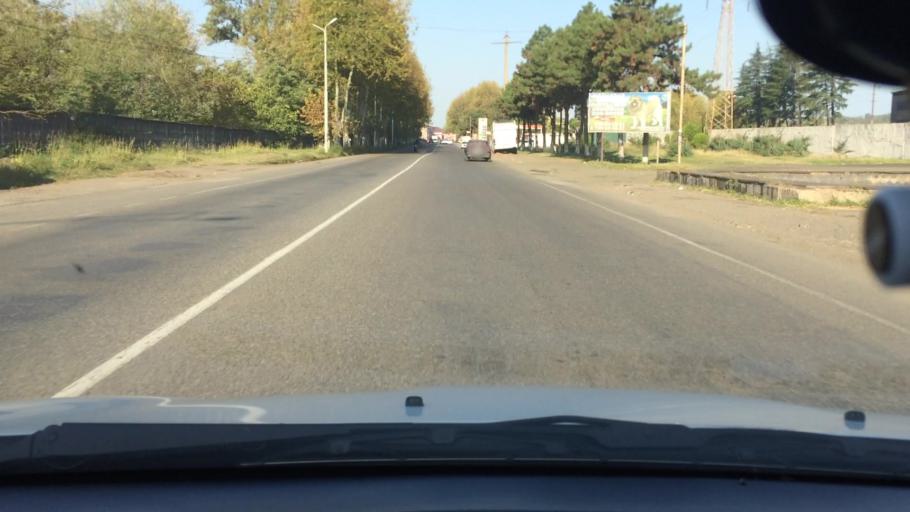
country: GE
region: Imereti
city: Zestap'oni
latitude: 42.1178
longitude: 43.0178
